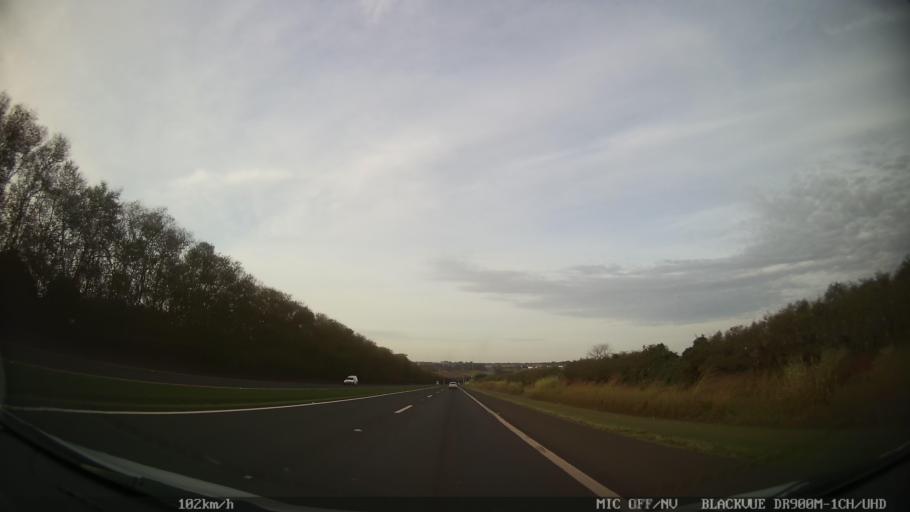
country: BR
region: Sao Paulo
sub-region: Iracemapolis
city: Iracemapolis
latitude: -22.6660
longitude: -47.5355
